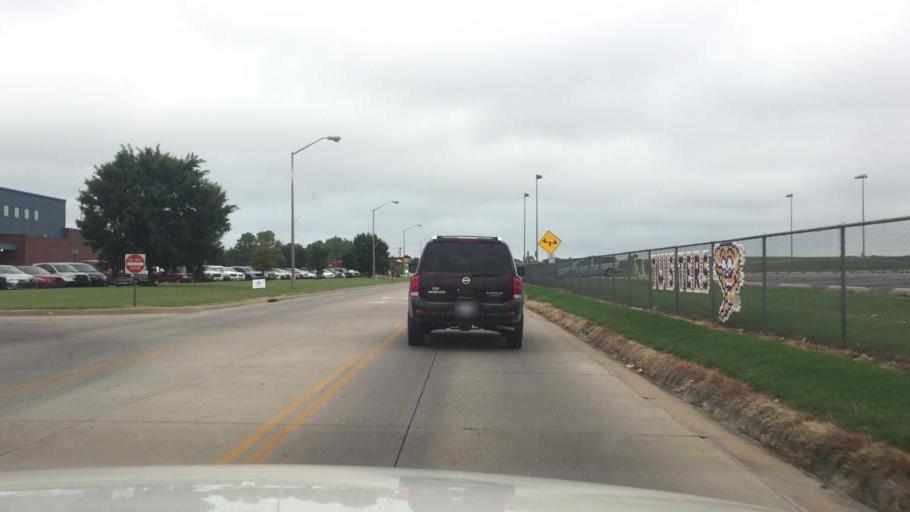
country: US
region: Kansas
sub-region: Montgomery County
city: Coffeyville
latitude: 37.0414
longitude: -95.6473
